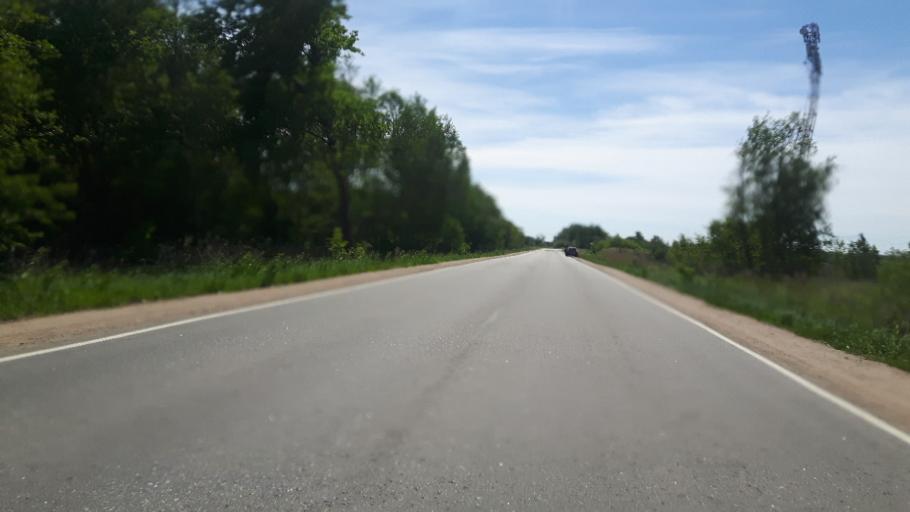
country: RU
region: Leningrad
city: Ust'-Luga
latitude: 59.5755
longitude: 28.1739
